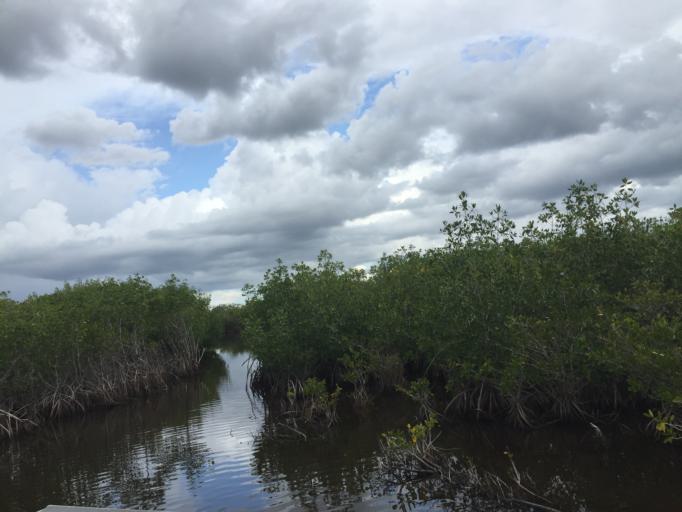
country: US
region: Florida
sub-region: Collier County
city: Marco
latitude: 25.9063
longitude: -81.3718
